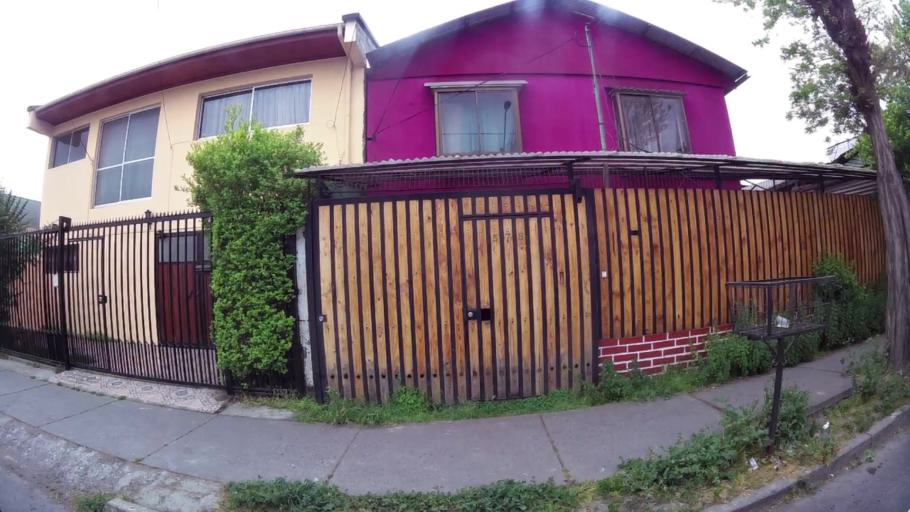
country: CL
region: Santiago Metropolitan
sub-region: Provincia de Santiago
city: Lo Prado
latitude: -33.5024
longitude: -70.7509
